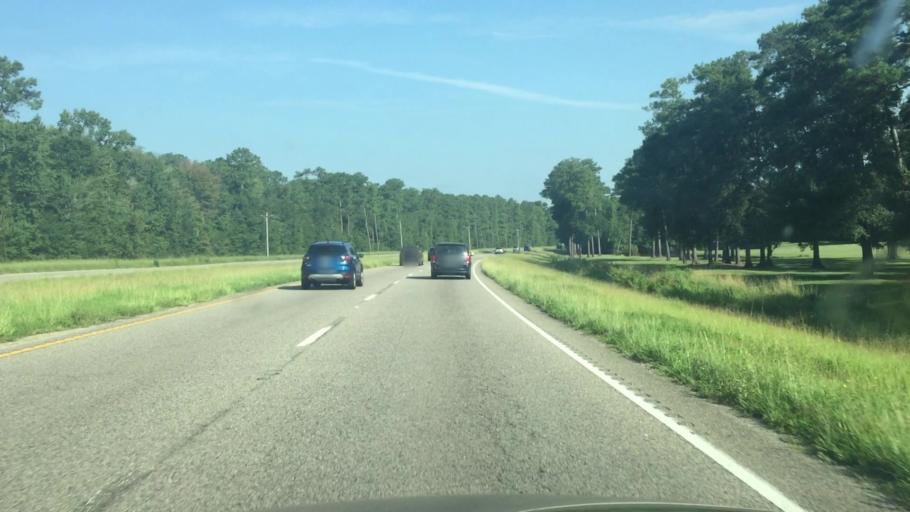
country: US
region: South Carolina
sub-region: Horry County
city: North Myrtle Beach
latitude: 33.9175
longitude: -78.7223
